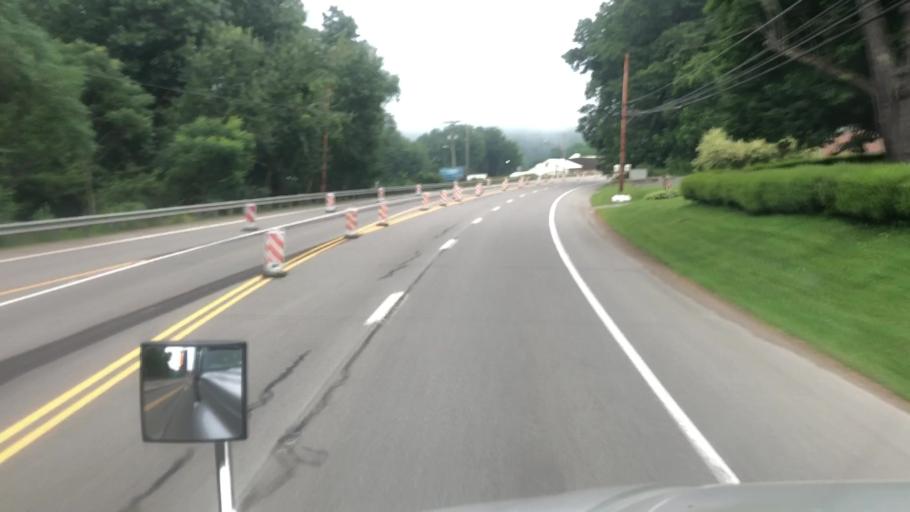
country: US
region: Pennsylvania
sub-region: Venango County
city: Woodland Heights
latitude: 41.4067
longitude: -79.7404
